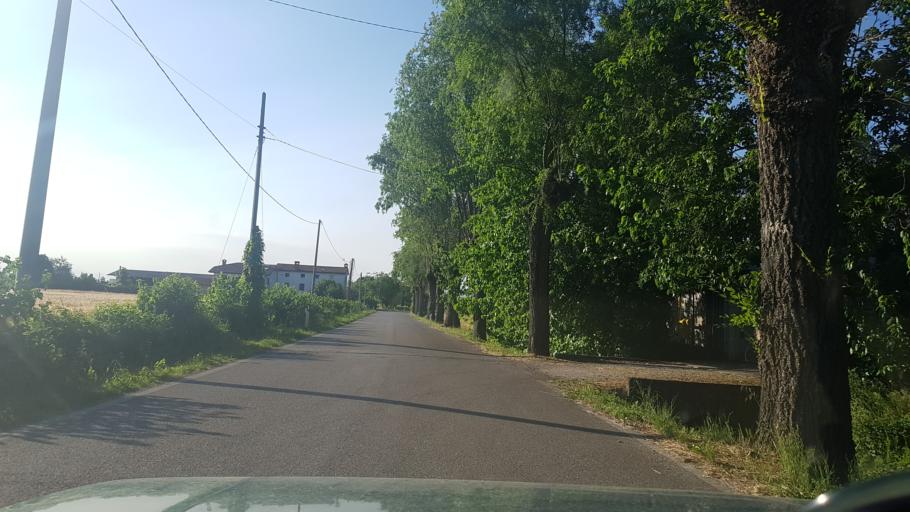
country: IT
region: Friuli Venezia Giulia
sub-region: Provincia di Gorizia
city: Farra d'Isonzo
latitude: 45.9153
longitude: 13.5193
